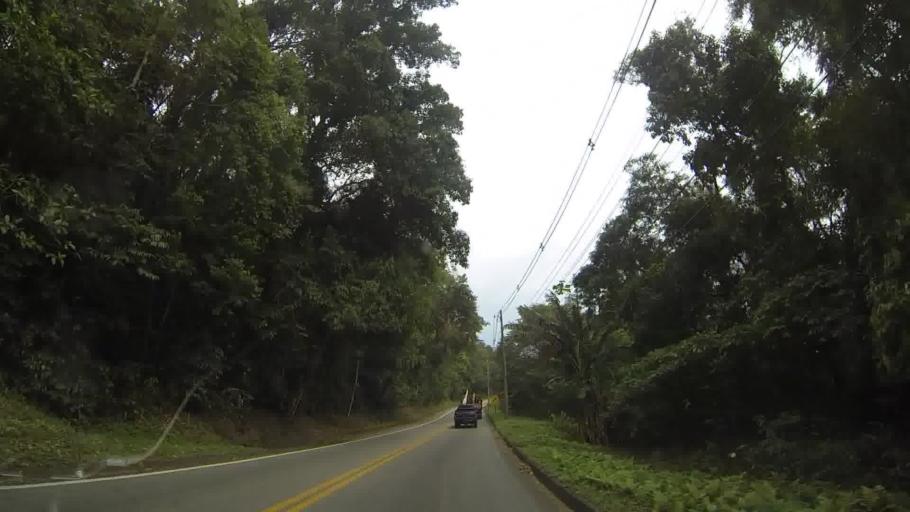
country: BR
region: Sao Paulo
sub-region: Sao Sebastiao
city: Sao Sebastiao
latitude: -23.8237
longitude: -45.5274
